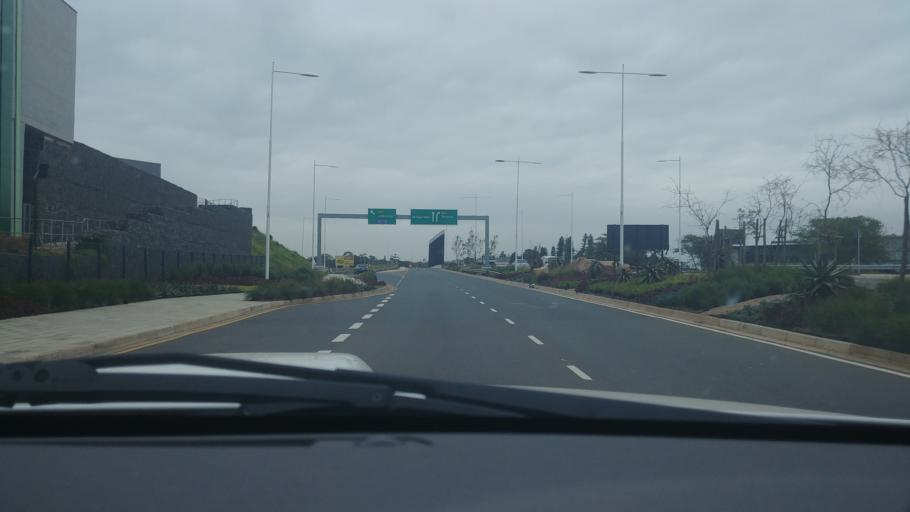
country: ZA
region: KwaZulu-Natal
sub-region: eThekwini Metropolitan Municipality
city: Durban
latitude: -29.7102
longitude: 31.0532
